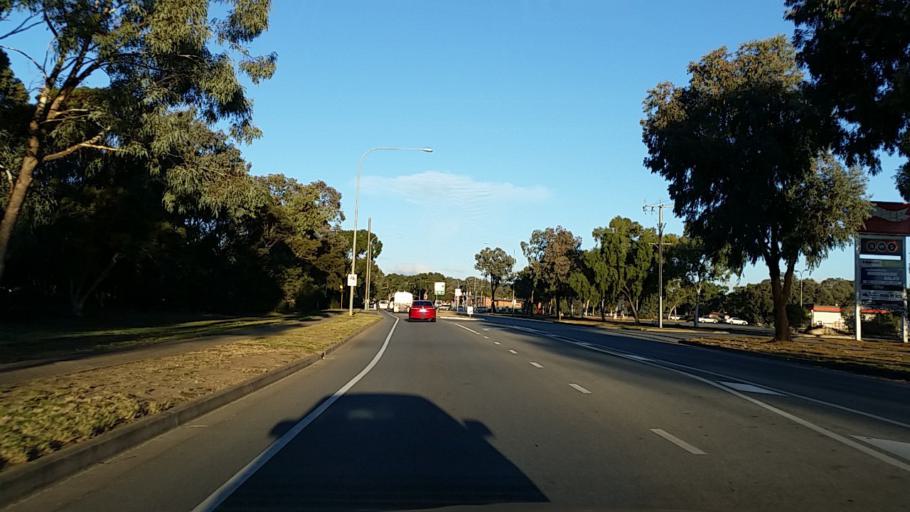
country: AU
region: South Australia
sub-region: Salisbury
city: Salisbury
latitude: -34.7650
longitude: 138.6674
